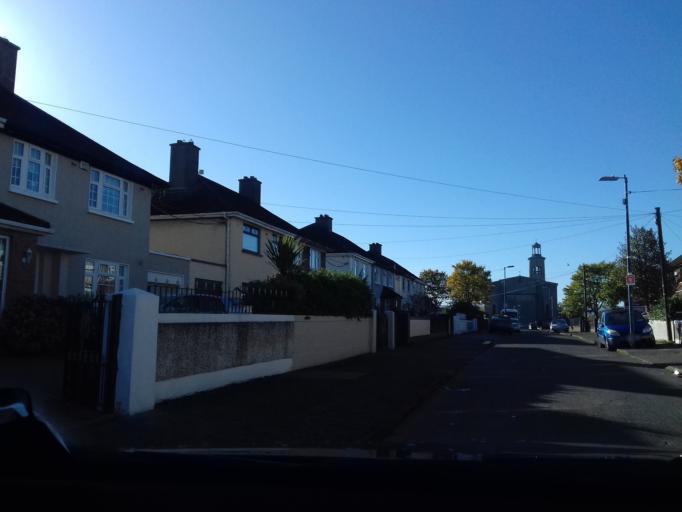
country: IE
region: Leinster
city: Cabra
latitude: 53.3698
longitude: -6.2952
